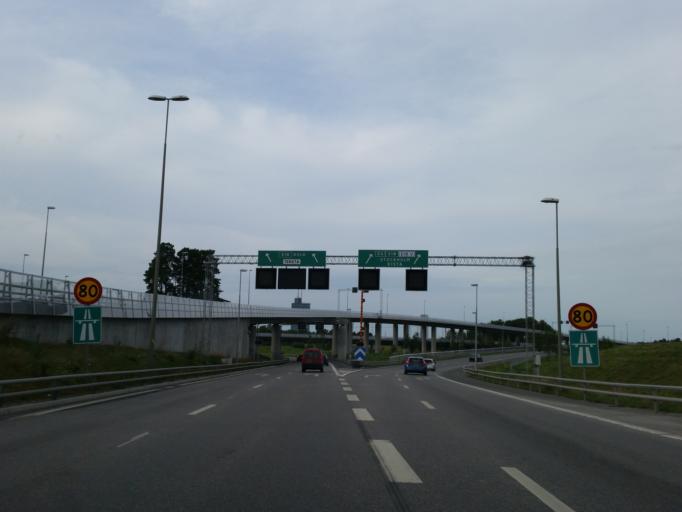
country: SE
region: Stockholm
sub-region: Stockholms Kommun
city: Kista
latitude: 59.3864
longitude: 17.9394
